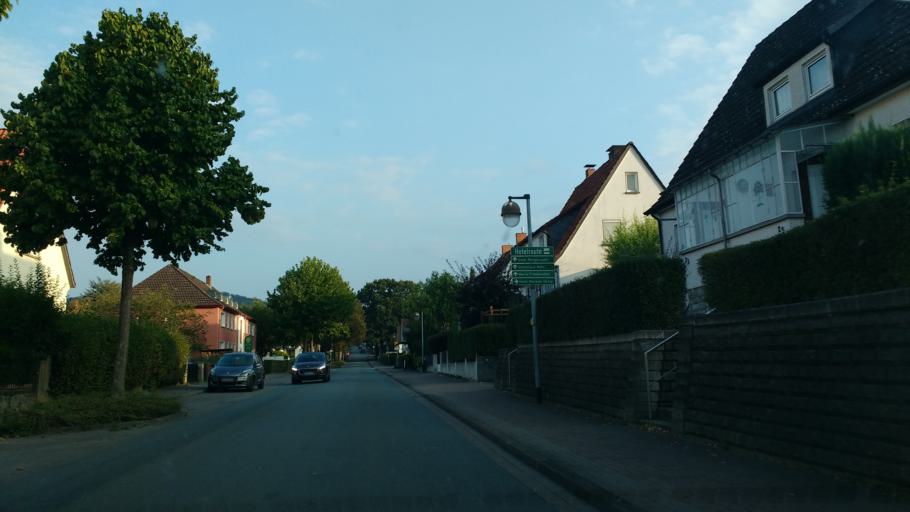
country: DE
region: Lower Saxony
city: Bad Pyrmont
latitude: 51.9806
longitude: 9.2672
